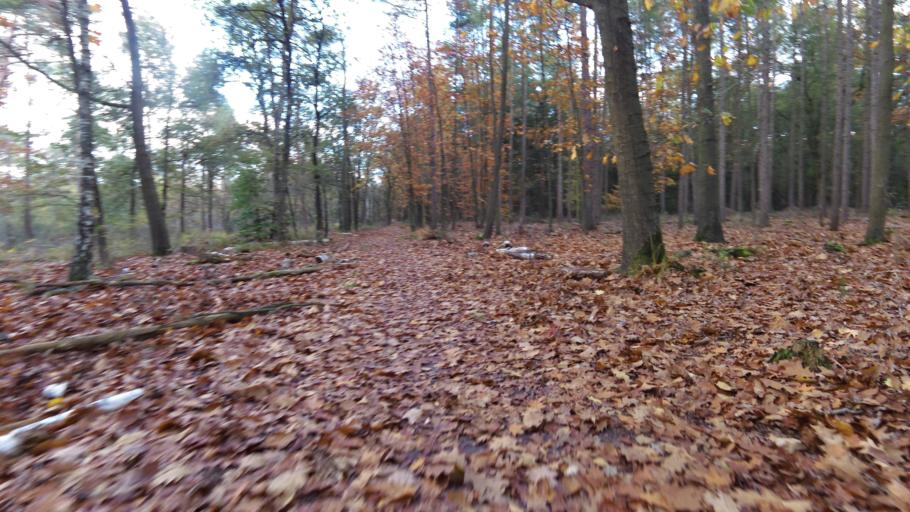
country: NL
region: Gelderland
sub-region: Gemeente Nunspeet
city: Nunspeet
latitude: 52.3520
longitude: 5.8265
